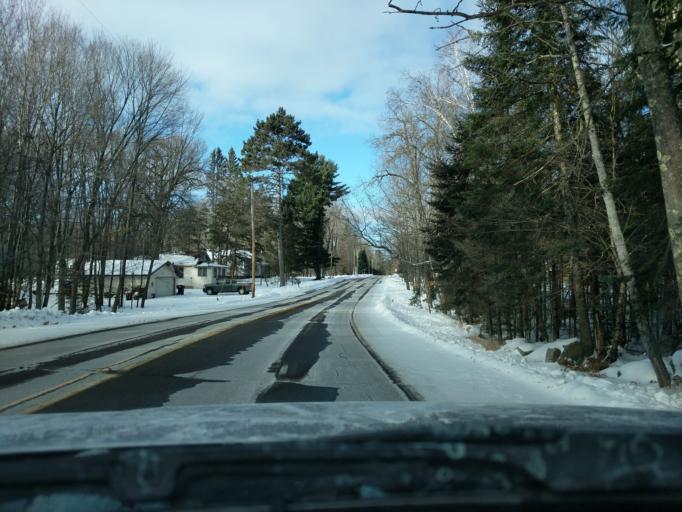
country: US
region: Wisconsin
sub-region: Vilas County
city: Eagle River
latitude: 45.7843
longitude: -89.0777
